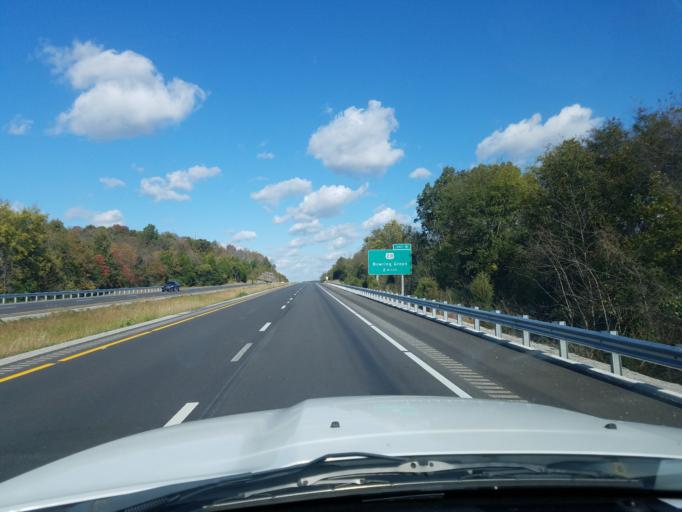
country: US
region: Kentucky
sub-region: Warren County
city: Bowling Green
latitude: 36.9645
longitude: -86.4983
